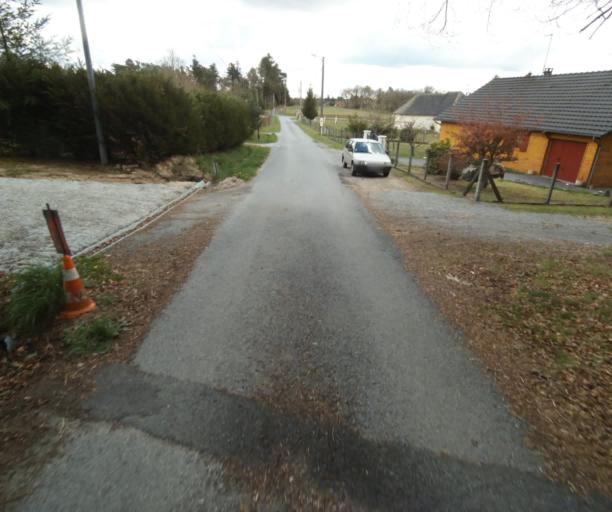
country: FR
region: Limousin
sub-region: Departement de la Correze
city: Correze
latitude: 45.2811
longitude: 1.9424
